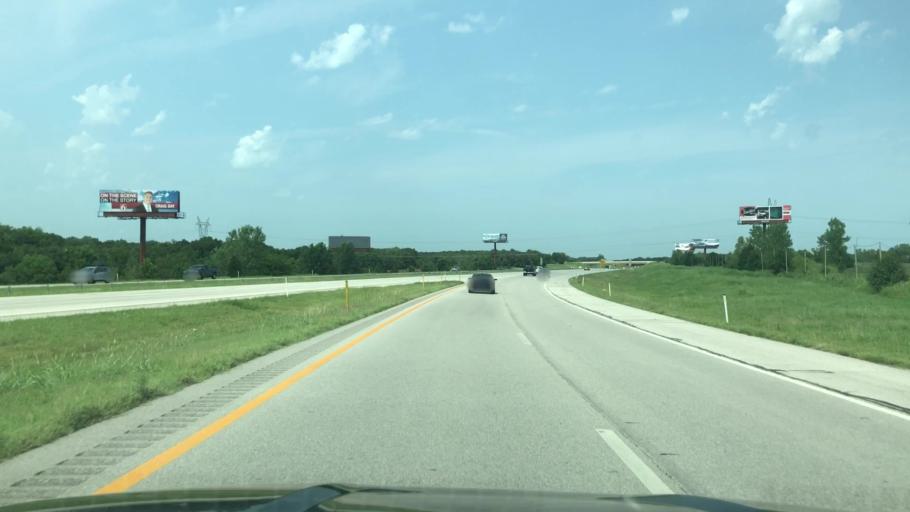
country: US
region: Oklahoma
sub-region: Rogers County
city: Catoosa
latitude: 36.1686
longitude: -95.7317
